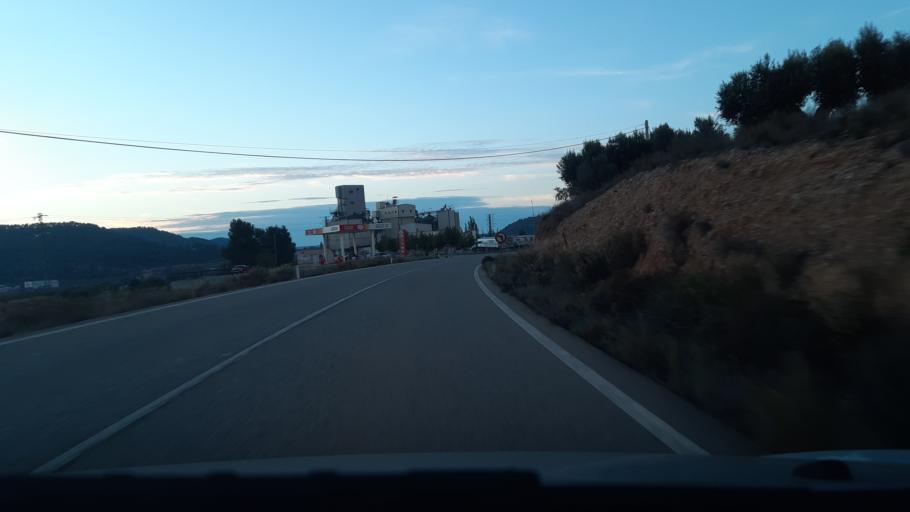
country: ES
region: Aragon
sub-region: Provincia de Teruel
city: Valderrobres
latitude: 40.8646
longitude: 0.1648
